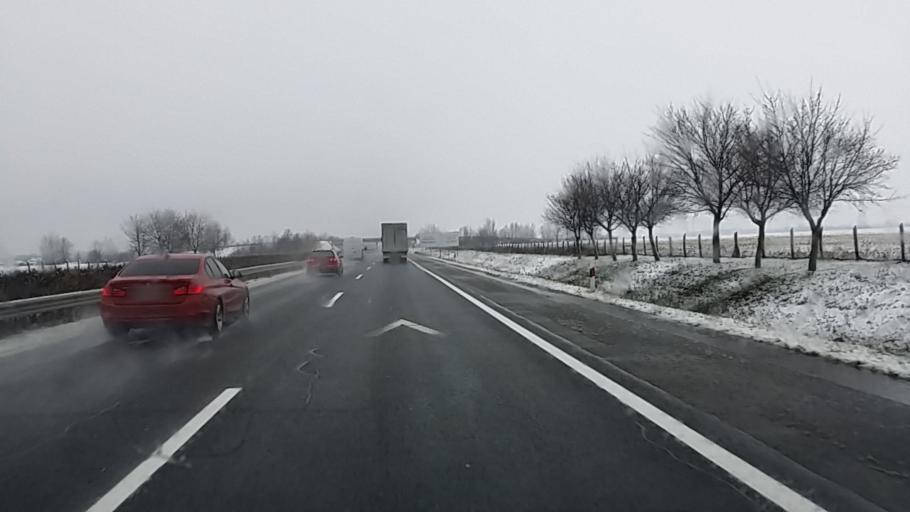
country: HU
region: Gyor-Moson-Sopron
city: Mosonszentmiklos
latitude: 47.7333
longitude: 17.4417
